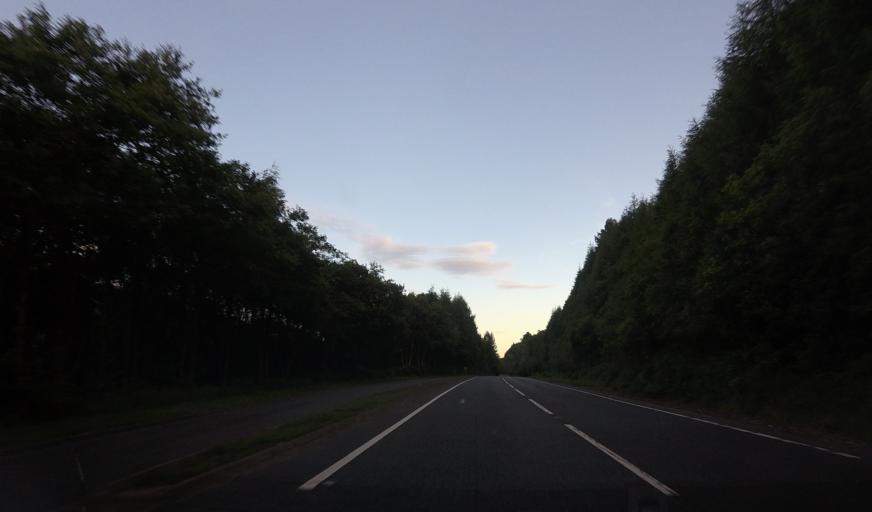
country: GB
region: Scotland
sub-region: Argyll and Bute
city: Garelochhead
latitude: 56.1822
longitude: -4.6918
